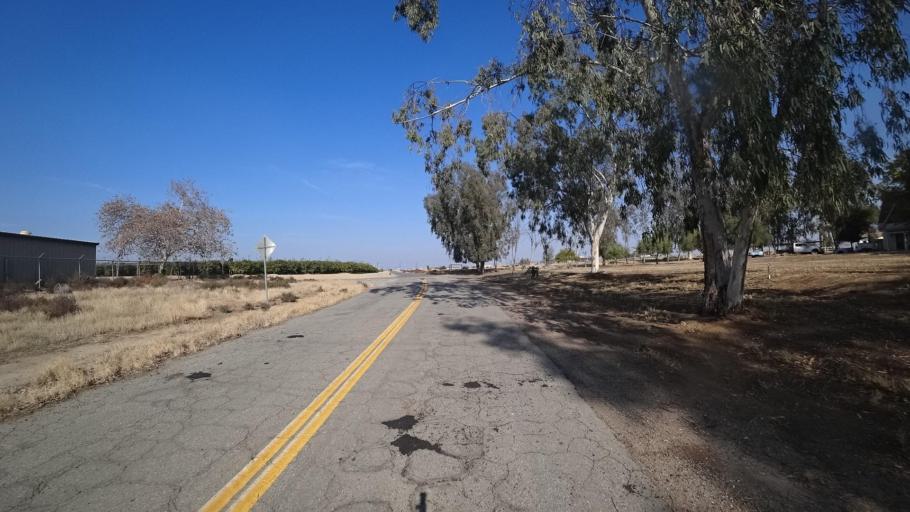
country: US
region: California
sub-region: Kern County
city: Oildale
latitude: 35.5229
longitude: -119.1088
